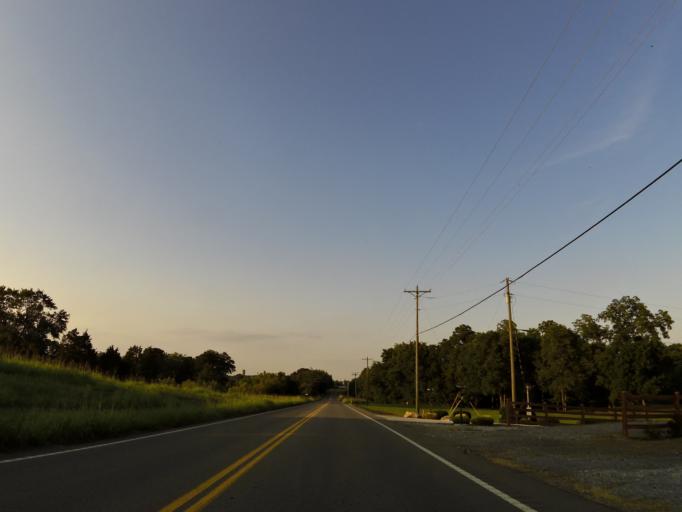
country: US
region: Tennessee
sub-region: Monroe County
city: Sweetwater
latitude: 35.5633
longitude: -84.5058
